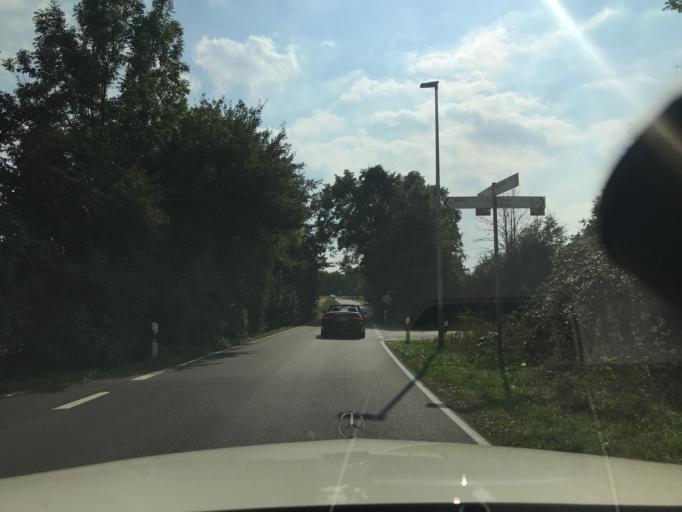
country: DE
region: North Rhine-Westphalia
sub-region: Regierungsbezirk Arnsberg
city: Werl
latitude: 51.5959
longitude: 7.8745
